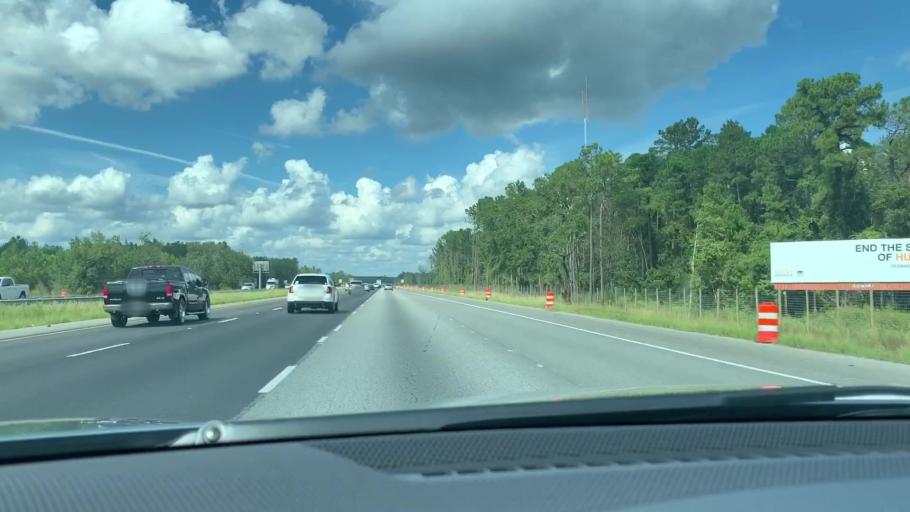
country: US
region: Georgia
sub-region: Camden County
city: Kingsland
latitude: 30.8547
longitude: -81.6757
